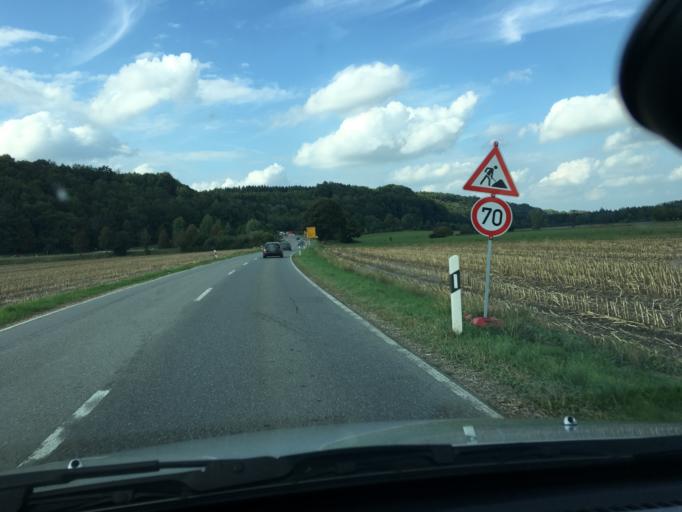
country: DE
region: Baden-Wuerttemberg
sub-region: Tuebingen Region
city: Hochdorf
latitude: 48.0461
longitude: 9.7980
